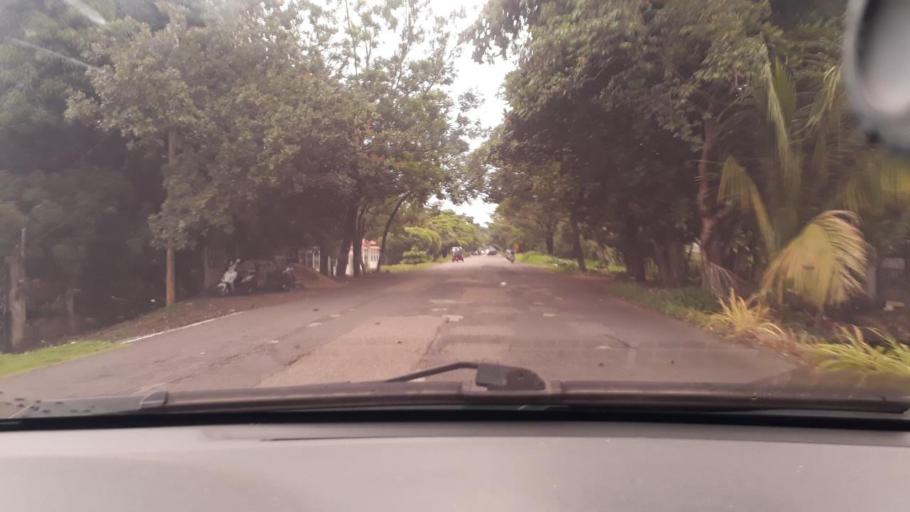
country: GT
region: Jutiapa
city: Jalpatagua
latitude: 14.1402
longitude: -90.0193
